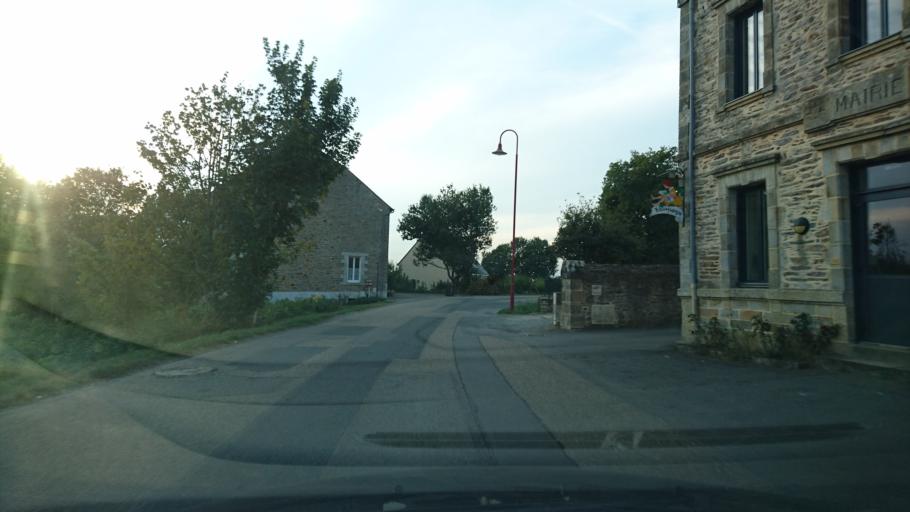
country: FR
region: Brittany
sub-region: Departement d'Ille-et-Vilaine
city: Saint-Just
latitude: 47.7660
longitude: -1.9624
